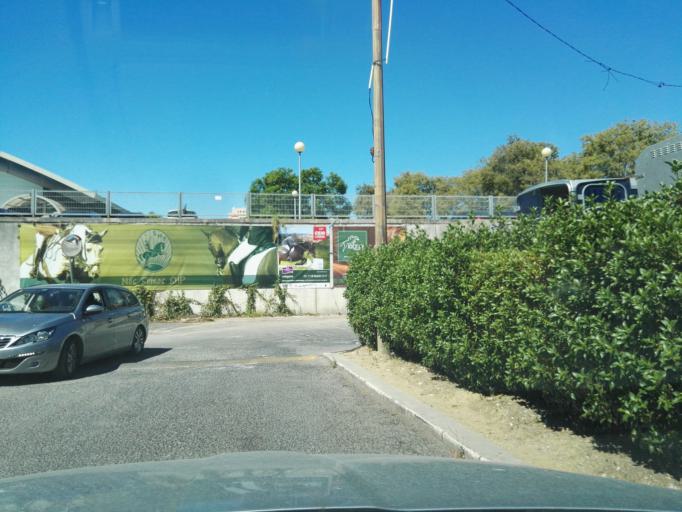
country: PT
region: Lisbon
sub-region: Odivelas
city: Olival do Basto
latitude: 38.7552
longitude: -9.1607
